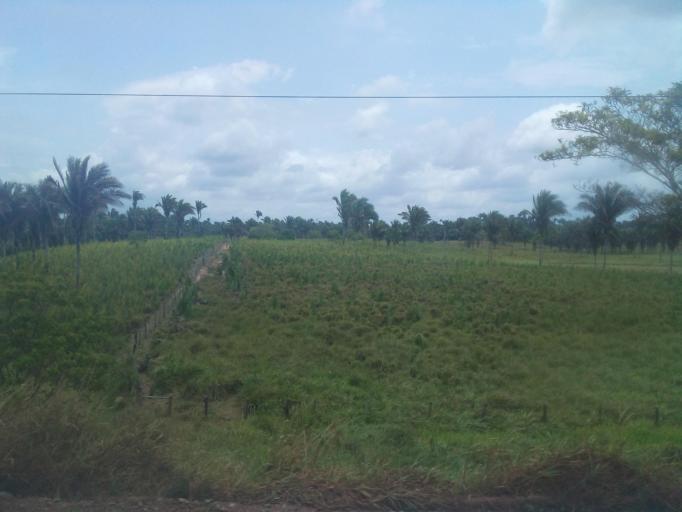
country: BR
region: Maranhao
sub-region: Santa Ines
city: Santa Ines
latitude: -3.6961
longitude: -45.6170
